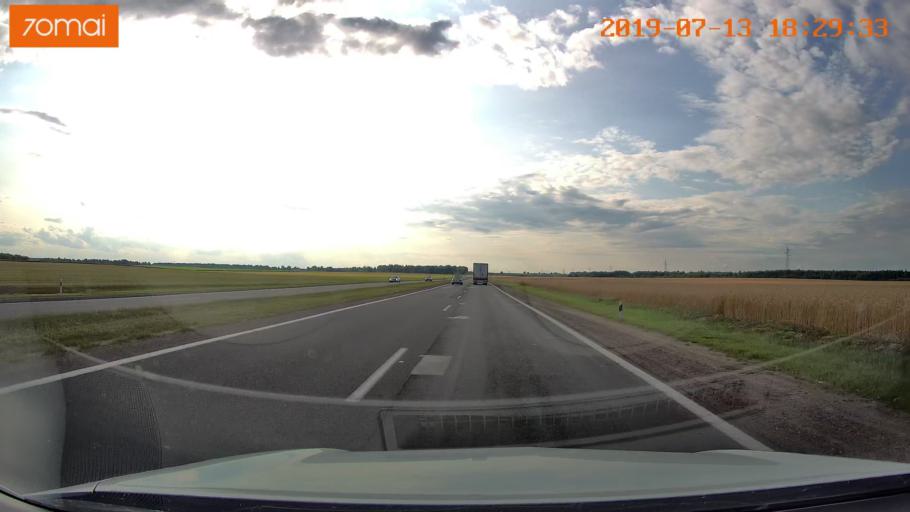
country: BY
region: Minsk
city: Dukora
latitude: 53.6527
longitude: 27.9674
